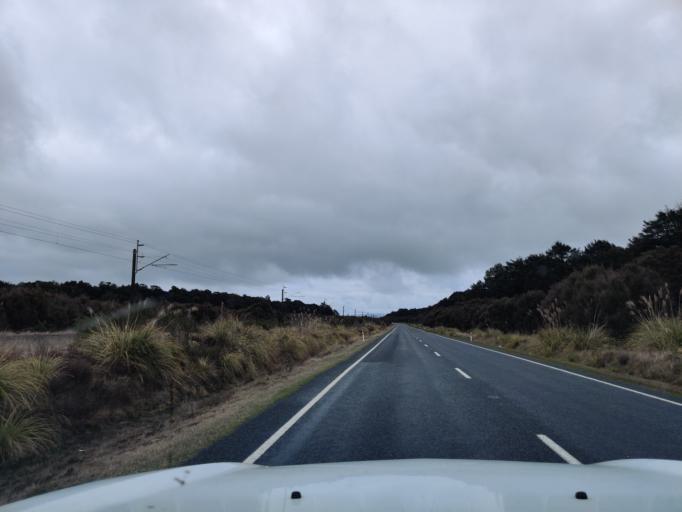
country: NZ
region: Manawatu-Wanganui
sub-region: Ruapehu District
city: Waiouru
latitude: -39.3264
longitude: 175.3837
